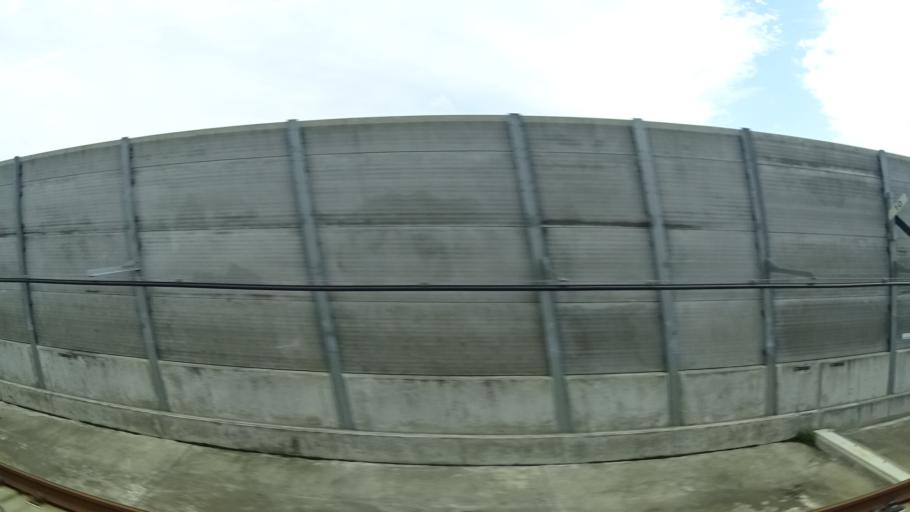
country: JP
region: Toyama
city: Nishishinminato
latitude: 36.7274
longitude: 137.0857
